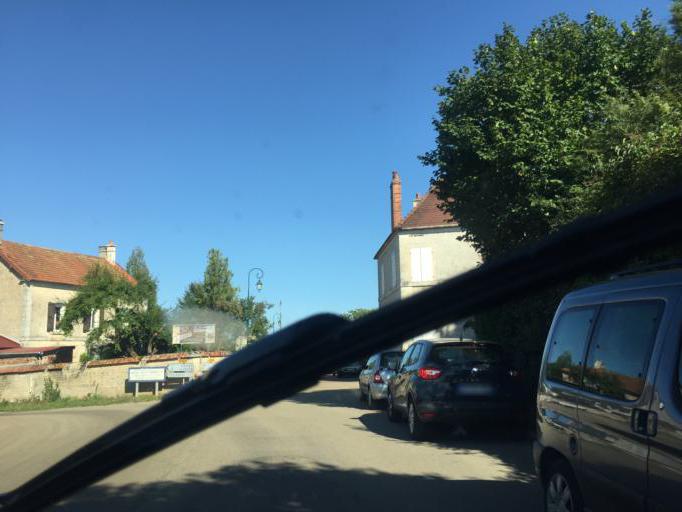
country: FR
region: Bourgogne
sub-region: Departement de l'Yonne
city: Fontenailles
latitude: 47.5035
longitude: 3.3486
